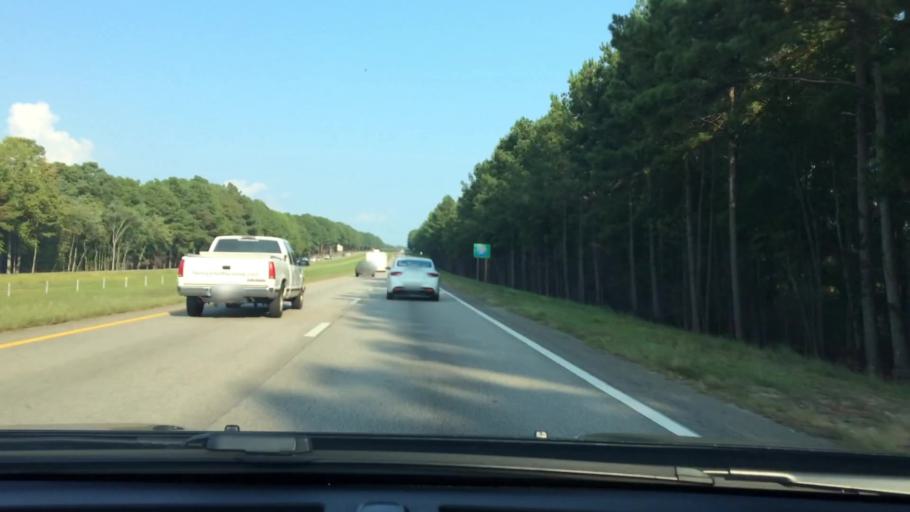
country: US
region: North Carolina
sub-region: Wake County
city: Zebulon
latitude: 35.8173
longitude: -78.2550
